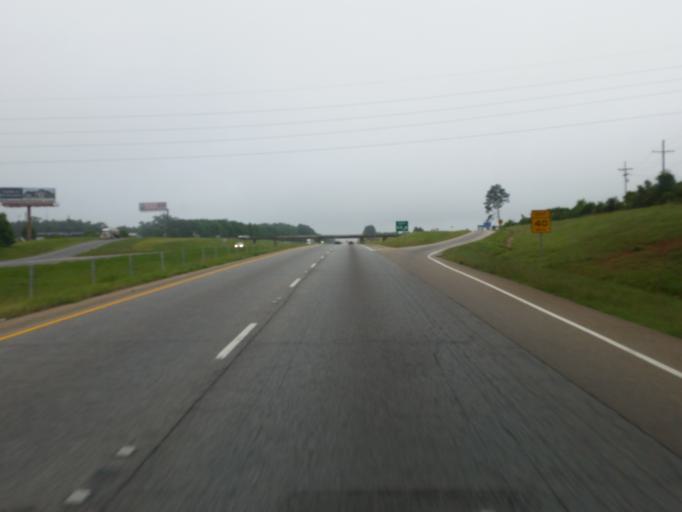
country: US
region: Louisiana
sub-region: Webster Parish
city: Minden
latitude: 32.5812
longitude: -93.2520
